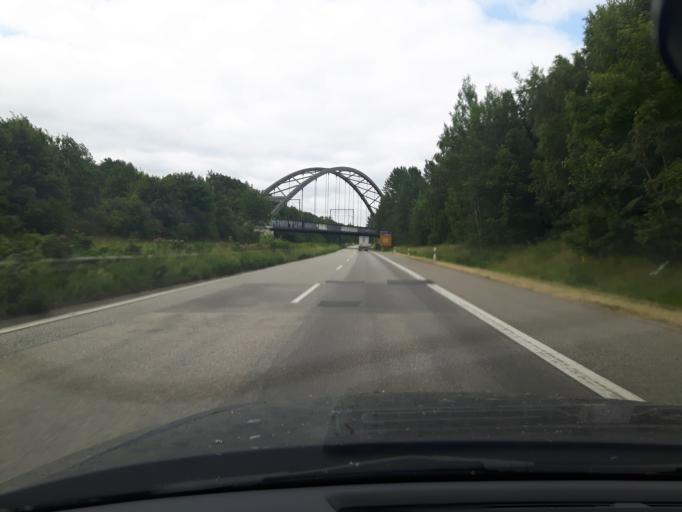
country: DE
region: Mecklenburg-Vorpommern
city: Selmsdorf
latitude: 53.9216
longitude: 10.8113
